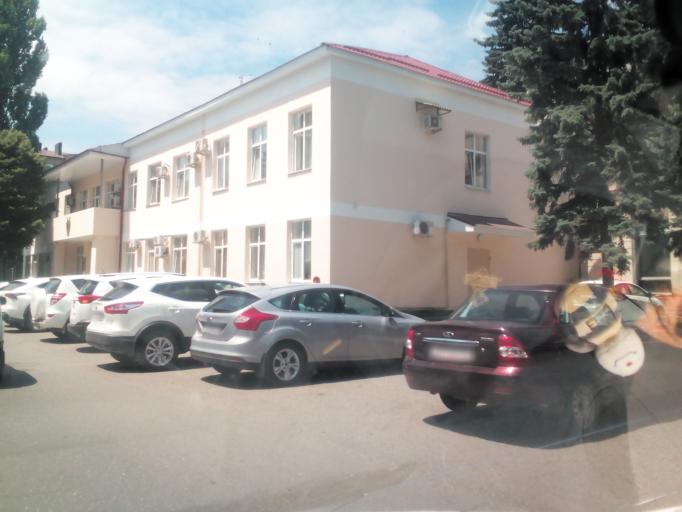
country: RU
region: Stavropol'skiy
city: Pyatigorsk
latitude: 44.0370
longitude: 43.0633
